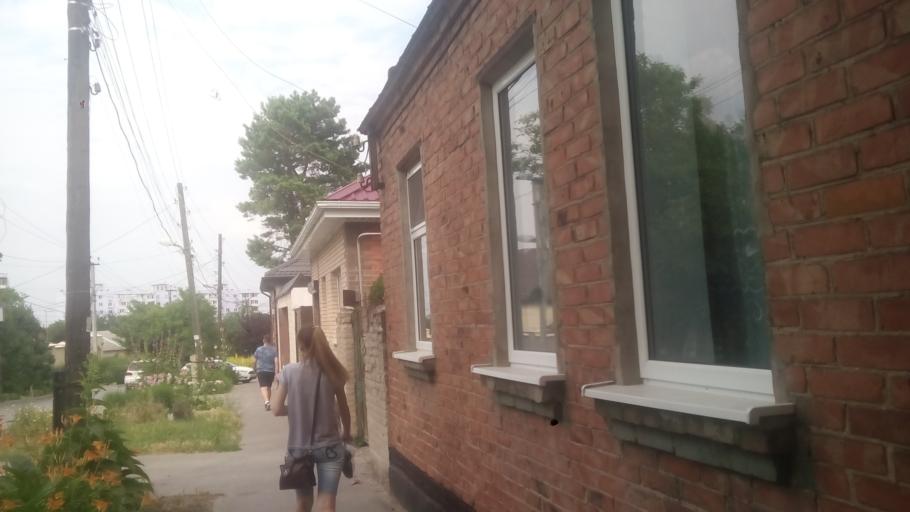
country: RU
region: Rostov
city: Rostov-na-Donu
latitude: 47.2175
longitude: 39.6594
